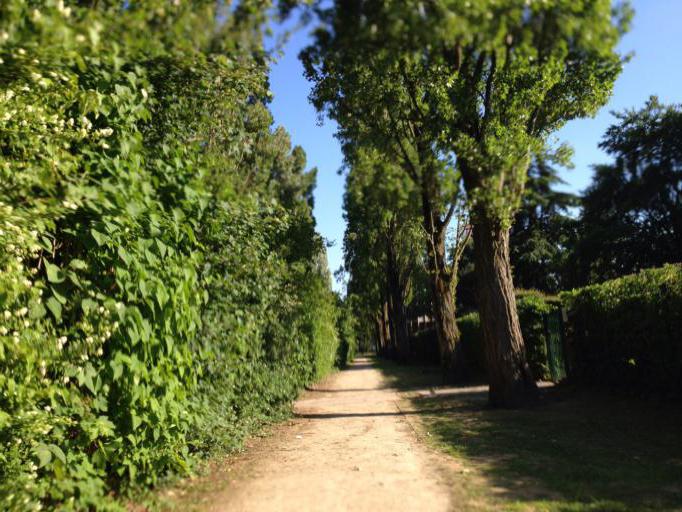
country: FR
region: Ile-de-France
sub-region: Departement des Hauts-de-Seine
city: Le Plessis-Robinson
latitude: 48.7907
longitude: 2.2522
